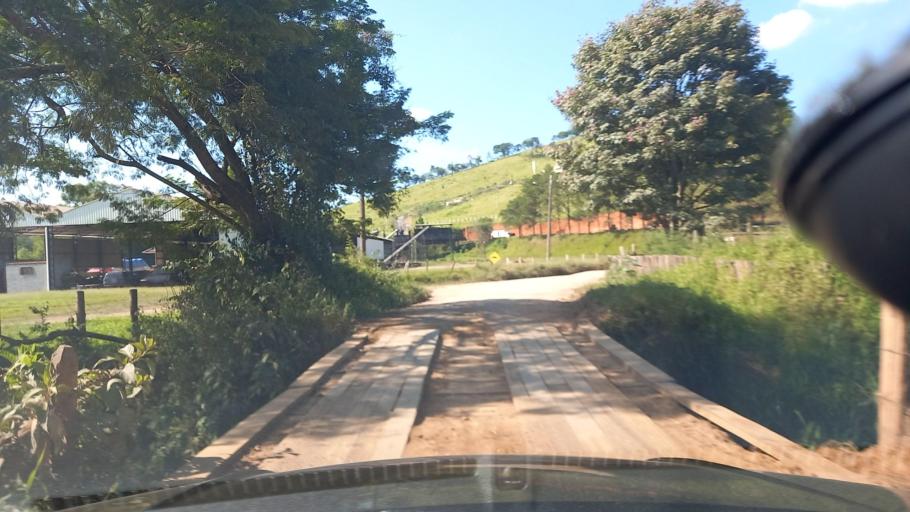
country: BR
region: Minas Gerais
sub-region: Camanducaia
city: Camanducaia
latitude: -22.7771
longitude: -46.1625
